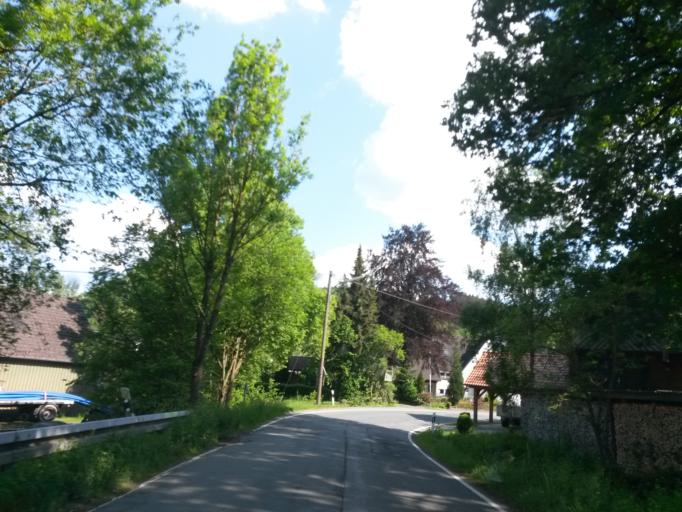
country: DE
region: North Rhine-Westphalia
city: Balve
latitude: 51.2899
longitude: 7.8482
